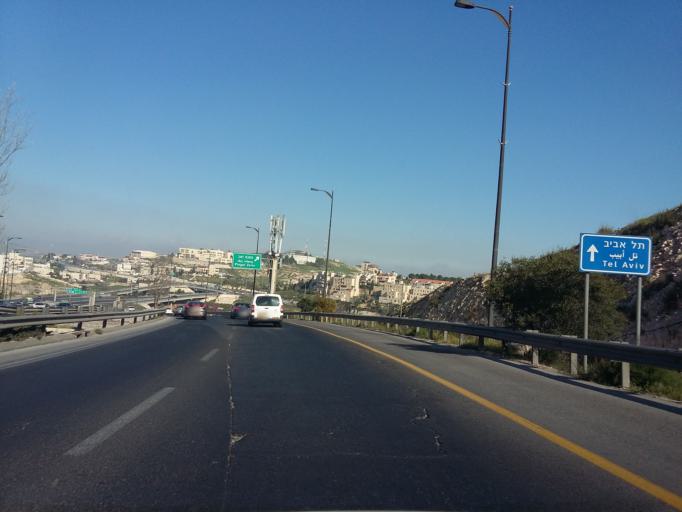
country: PS
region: West Bank
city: `Anata
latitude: 31.8150
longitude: 35.2381
